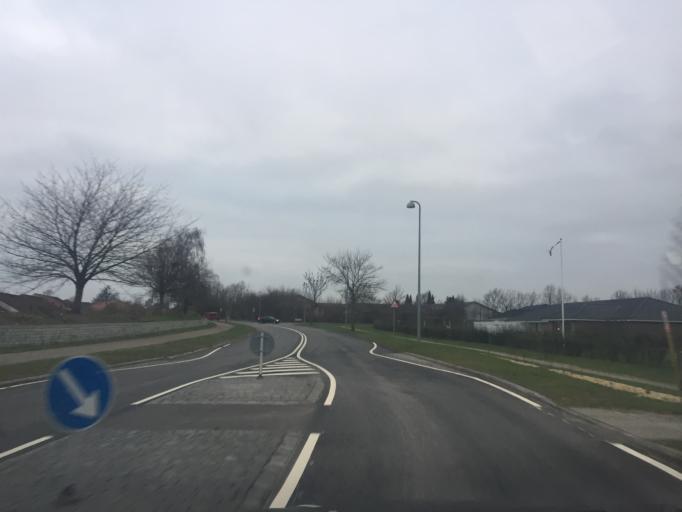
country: DK
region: Zealand
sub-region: Roskilde Kommune
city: Gundsomagle
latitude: 55.7362
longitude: 12.1602
